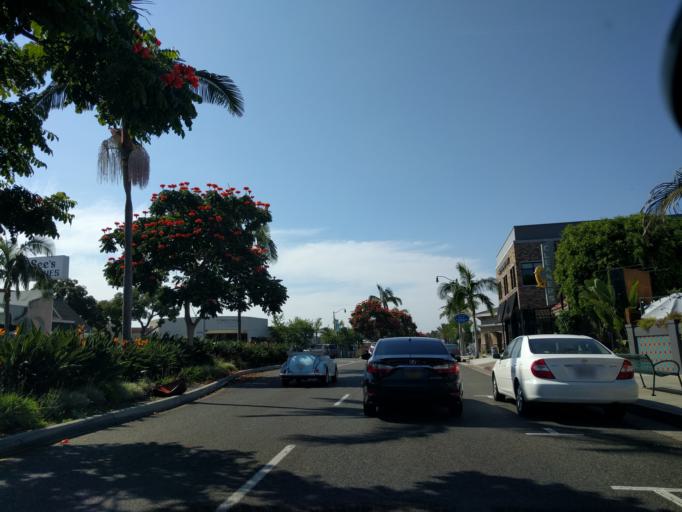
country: US
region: California
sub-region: Orange County
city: San Joaquin Hills
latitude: 33.5949
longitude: -117.8689
